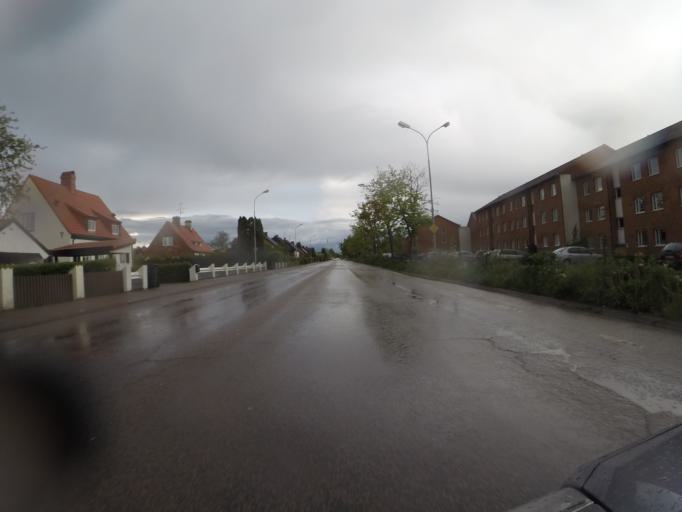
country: SE
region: Skane
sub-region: Bjuvs Kommun
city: Bjuv
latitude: 56.0806
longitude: 12.9274
